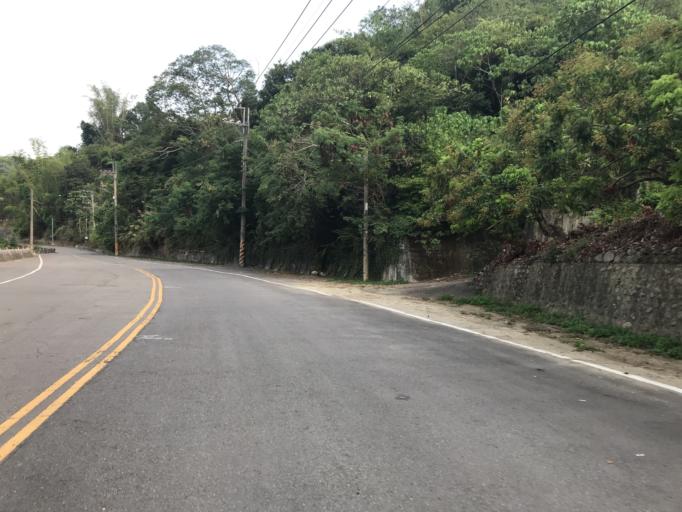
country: TW
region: Taiwan
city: Zhongxing New Village
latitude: 24.0394
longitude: 120.7080
